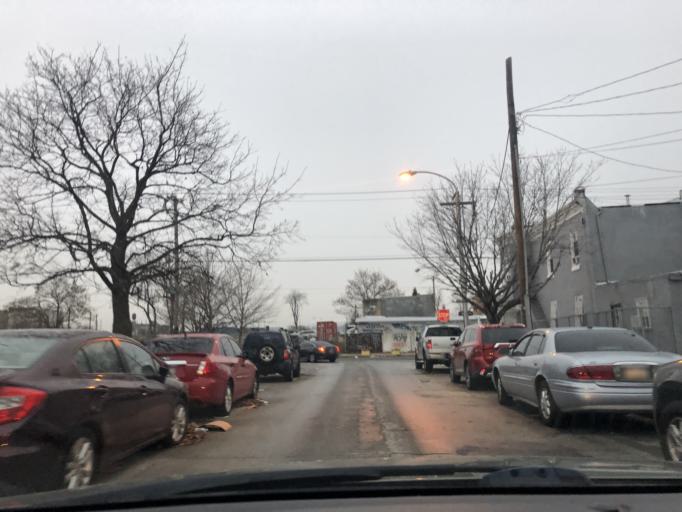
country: US
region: Pennsylvania
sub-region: Philadelphia County
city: Philadelphia
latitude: 39.9958
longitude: -75.1352
